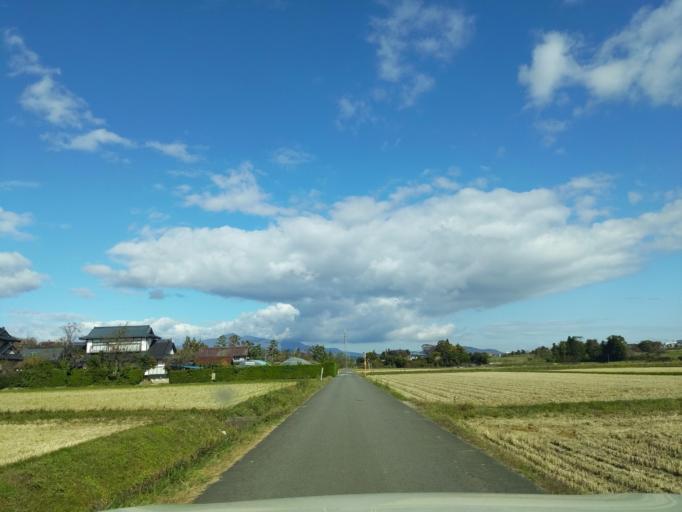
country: JP
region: Fukushima
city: Koriyama
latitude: 37.4255
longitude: 140.3288
